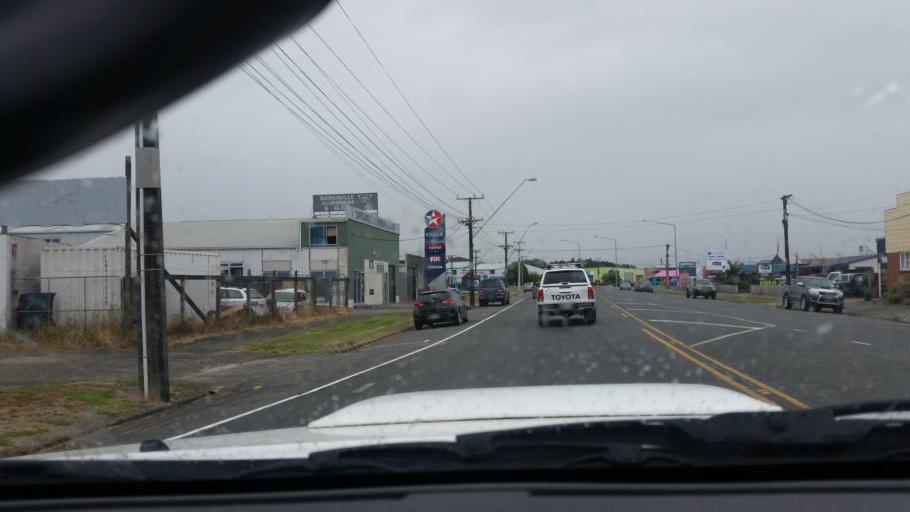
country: NZ
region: Northland
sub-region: Kaipara District
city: Dargaville
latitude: -35.9427
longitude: 173.8671
